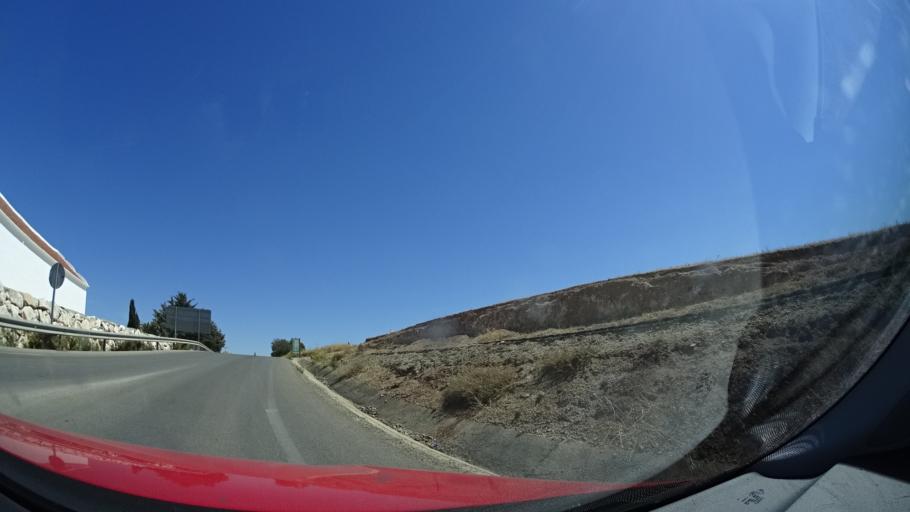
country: ES
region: Andalusia
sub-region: Provincia de Malaga
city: Sierra de Yeguas
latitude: 37.1242
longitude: -4.8761
